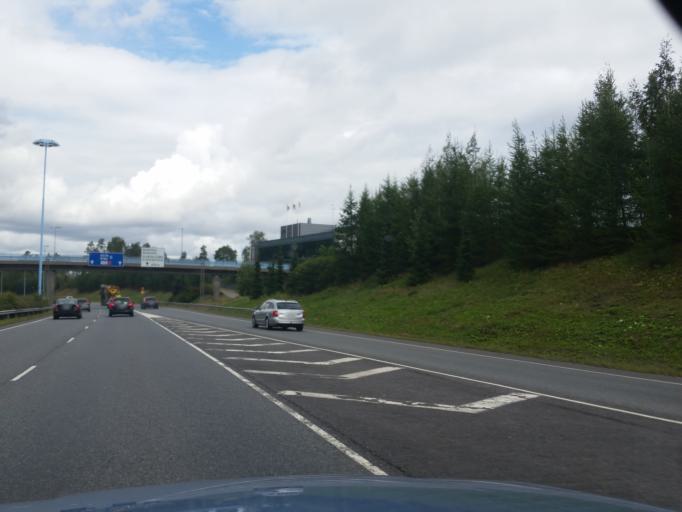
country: FI
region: Uusimaa
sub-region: Helsinki
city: Koukkuniemi
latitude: 60.1730
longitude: 24.7549
